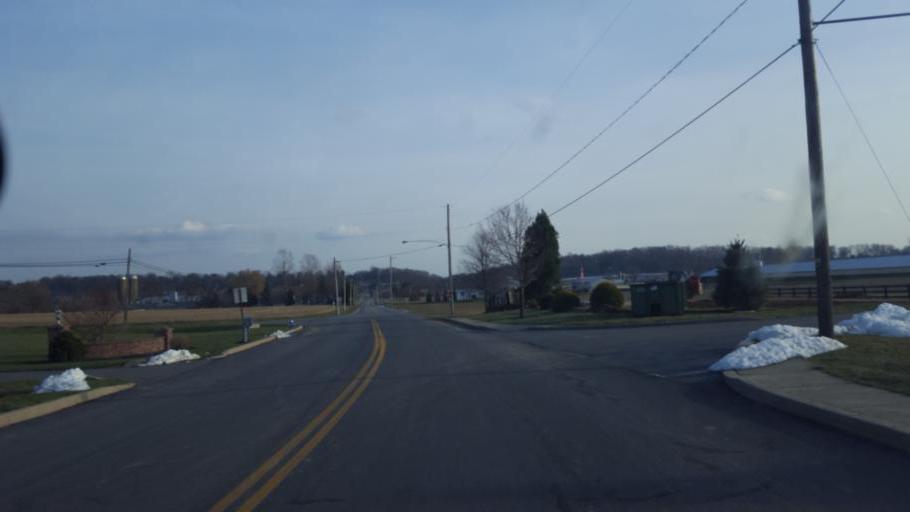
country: US
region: Pennsylvania
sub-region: Lancaster County
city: New Holland
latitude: 40.0881
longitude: -76.0886
